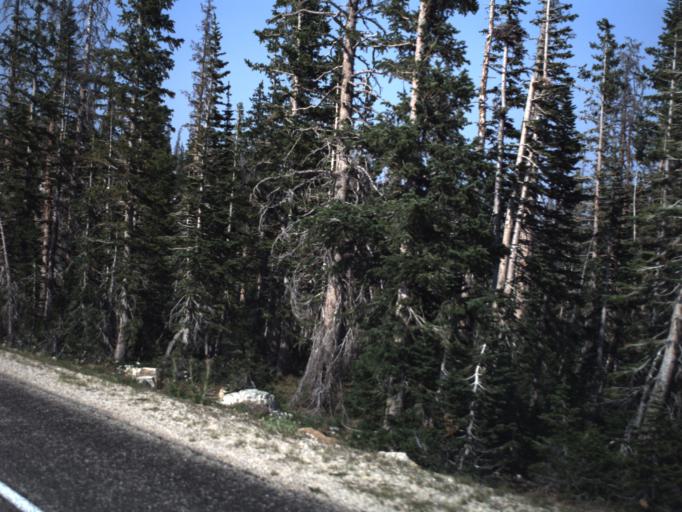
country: US
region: Utah
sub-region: Summit County
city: Kamas
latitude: 40.6910
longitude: -110.8974
